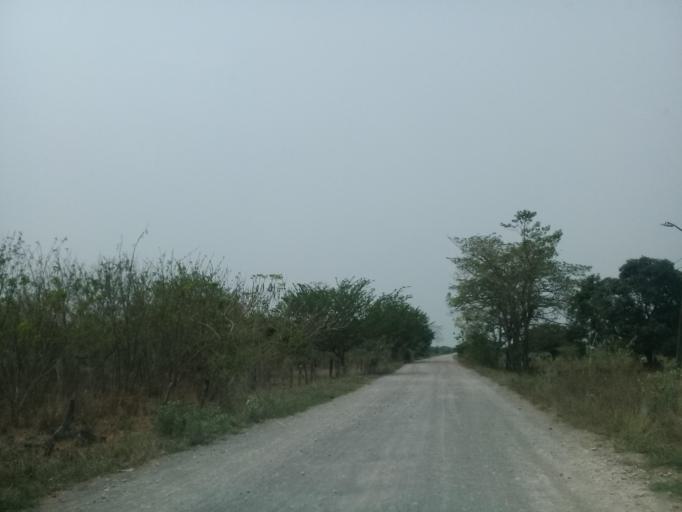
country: MX
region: Veracruz
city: Jamapa
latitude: 18.9351
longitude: -96.2169
